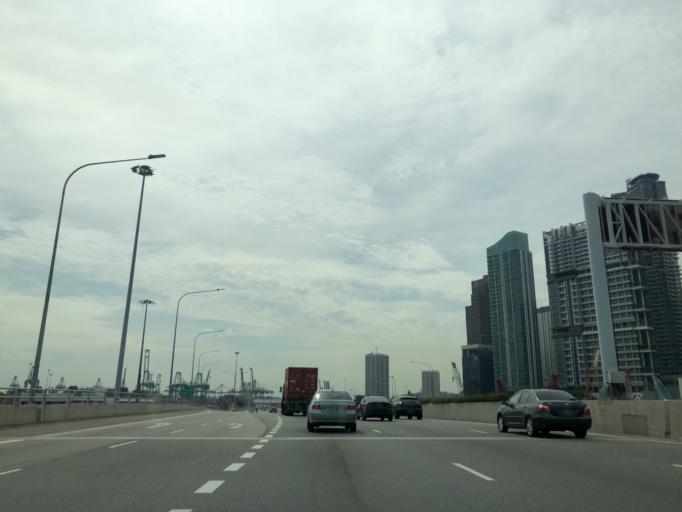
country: SG
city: Singapore
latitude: 1.2735
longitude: 103.8500
